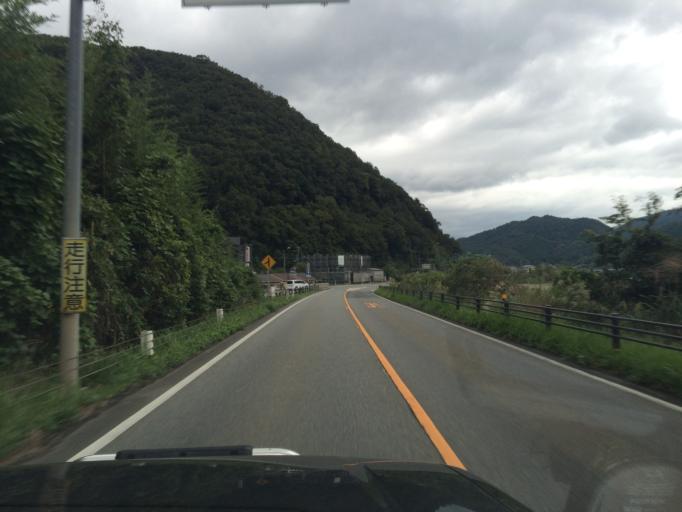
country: JP
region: Hyogo
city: Toyooka
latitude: 35.4163
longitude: 134.7840
